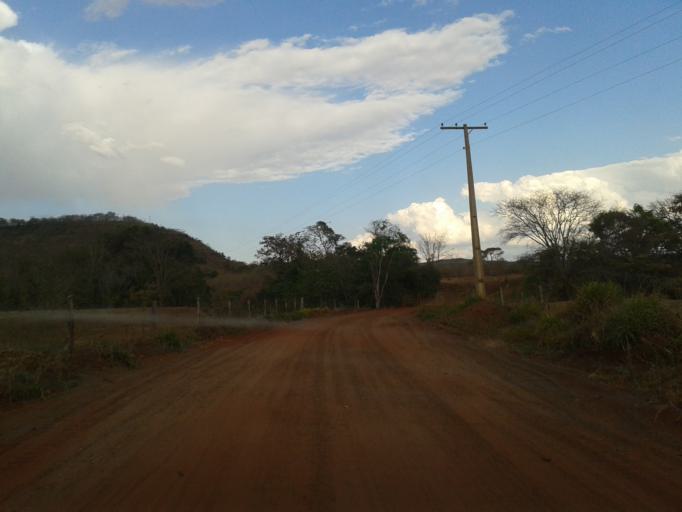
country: BR
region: Minas Gerais
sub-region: Santa Vitoria
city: Santa Vitoria
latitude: -19.2023
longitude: -49.8903
